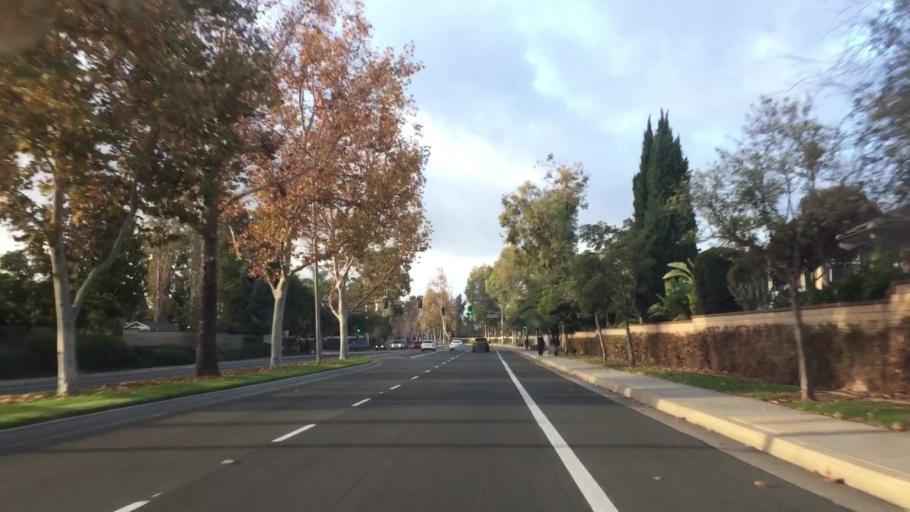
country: US
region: California
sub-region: Orange County
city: North Tustin
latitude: 33.7082
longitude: -117.7703
